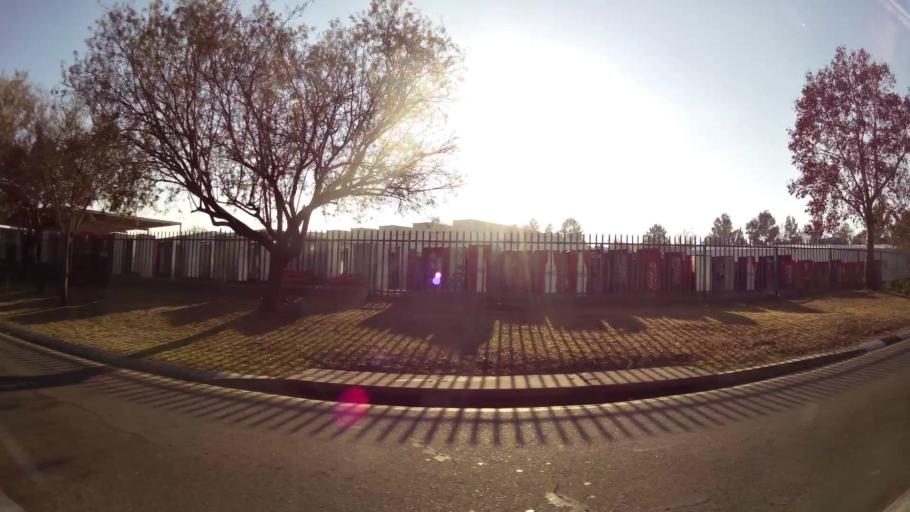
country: ZA
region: Gauteng
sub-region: City of Johannesburg Metropolitan Municipality
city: Modderfontein
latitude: -26.0782
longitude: 28.1156
